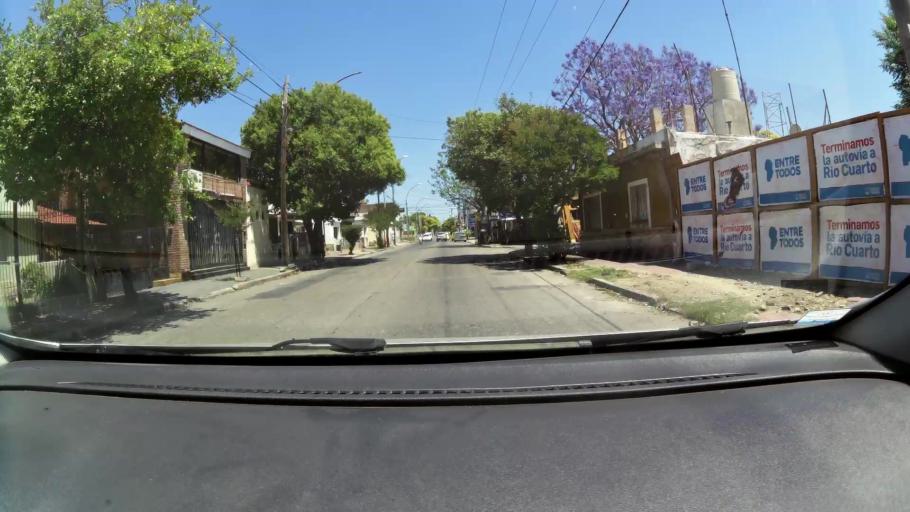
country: AR
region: Cordoba
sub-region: Departamento de Capital
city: Cordoba
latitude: -31.4147
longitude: -64.2198
